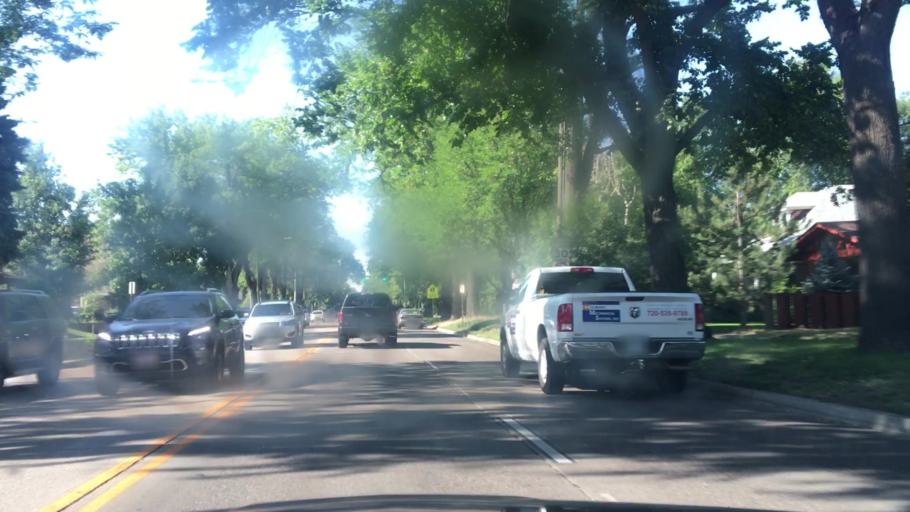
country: US
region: Colorado
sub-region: Arapahoe County
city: Glendale
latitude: 39.6963
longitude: -104.9593
